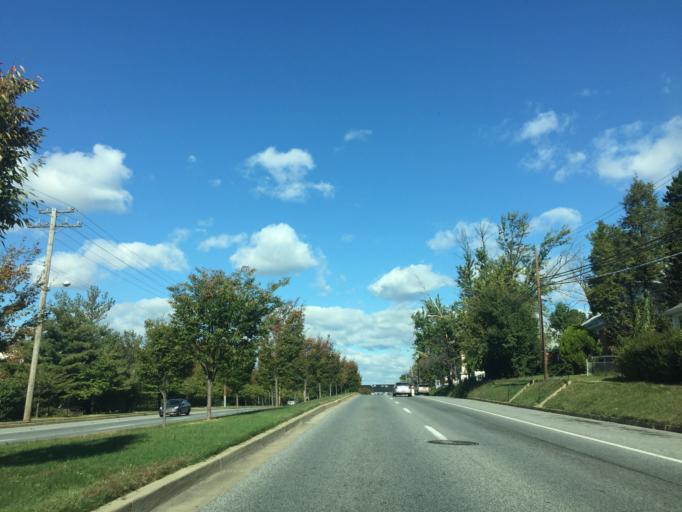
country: US
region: Maryland
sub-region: Baltimore County
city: Dundalk
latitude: 39.2676
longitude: -76.5286
